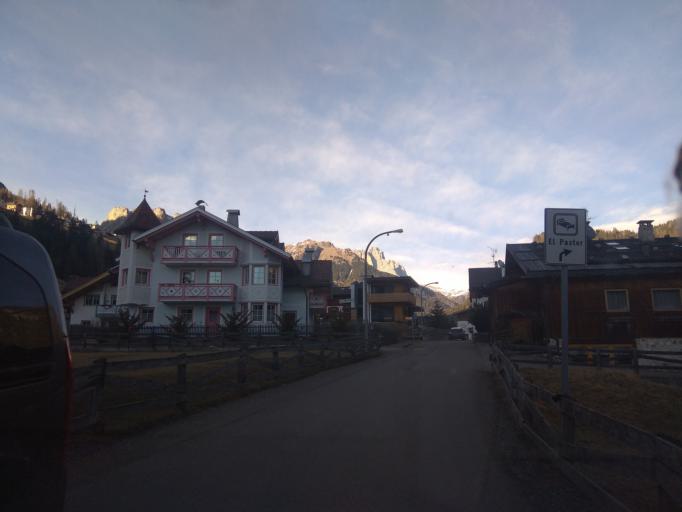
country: IT
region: Trentino-Alto Adige
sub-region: Provincia di Trento
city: Pozza di Fassa
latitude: 46.4403
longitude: 11.6921
